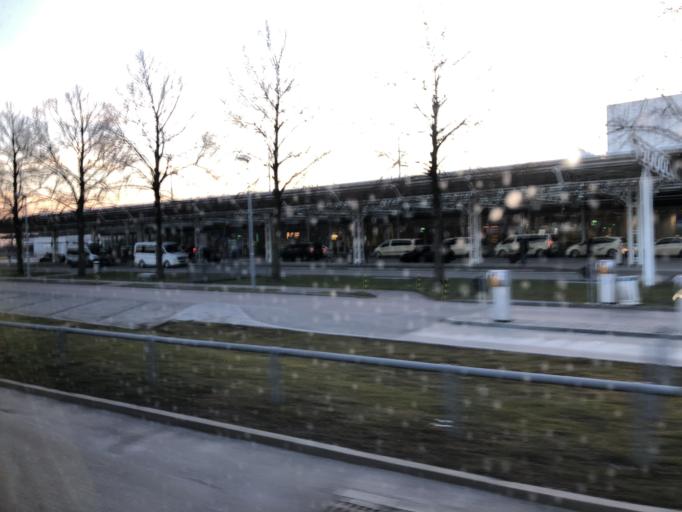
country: DE
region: Bavaria
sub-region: Upper Bavaria
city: Hallbergmoos
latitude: 48.3506
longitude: 11.7855
